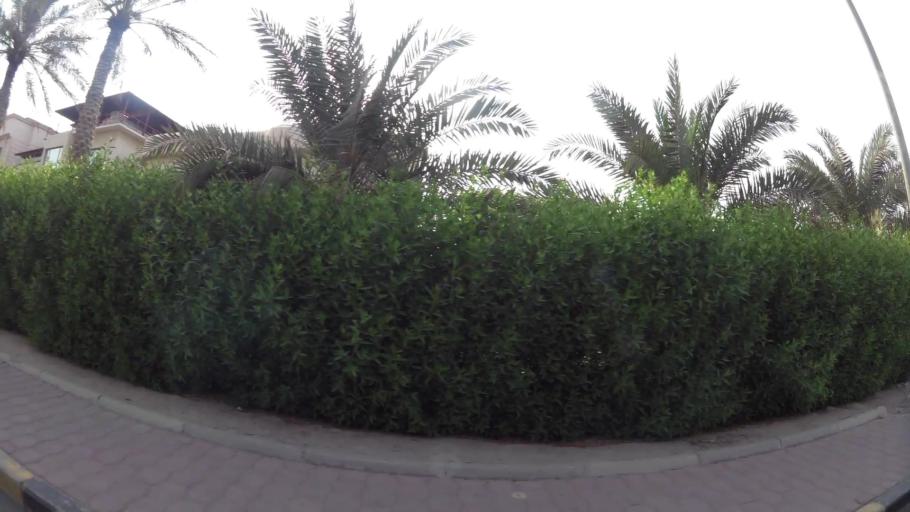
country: KW
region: Mubarak al Kabir
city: Sabah as Salim
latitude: 29.2248
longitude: 48.0602
